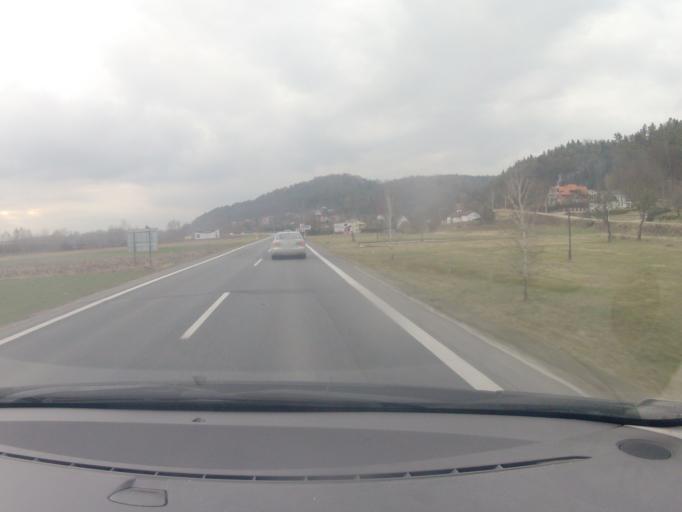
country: PL
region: Subcarpathian Voivodeship
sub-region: Powiat jasielski
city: Jaslo
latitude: 49.7736
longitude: 21.4522
